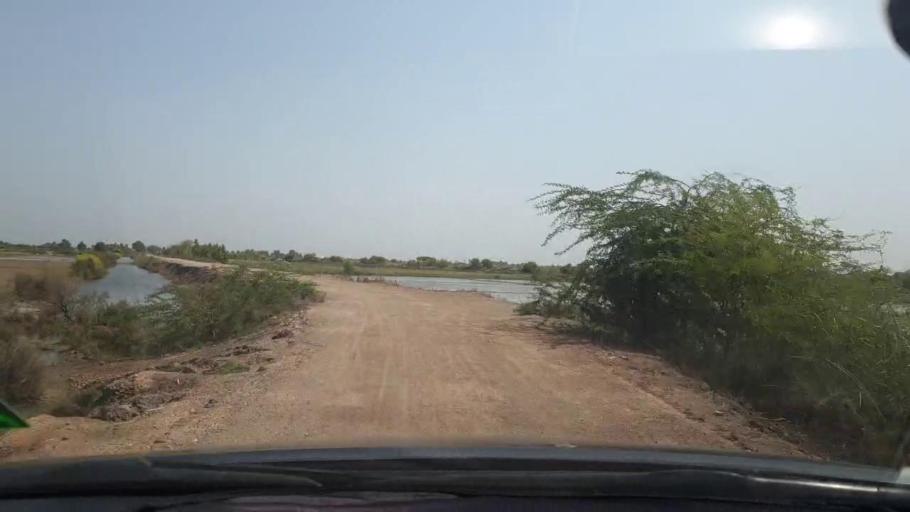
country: PK
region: Sindh
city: Tando Bago
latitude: 24.7940
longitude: 69.0948
